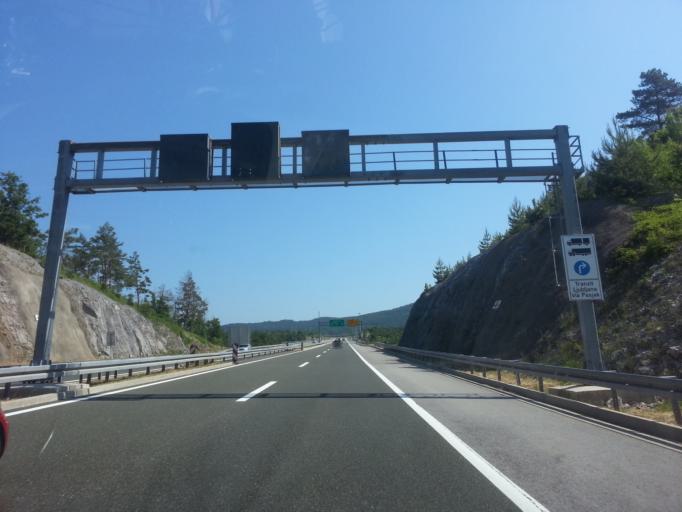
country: HR
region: Primorsko-Goranska
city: Klana
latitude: 45.4663
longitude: 14.2713
